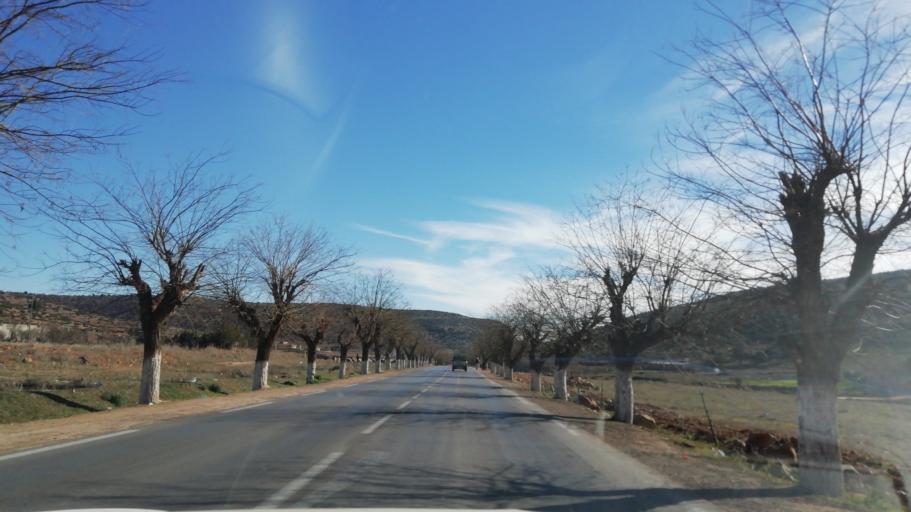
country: DZ
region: Tlemcen
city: Sebdou
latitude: 34.7060
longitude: -1.3187
